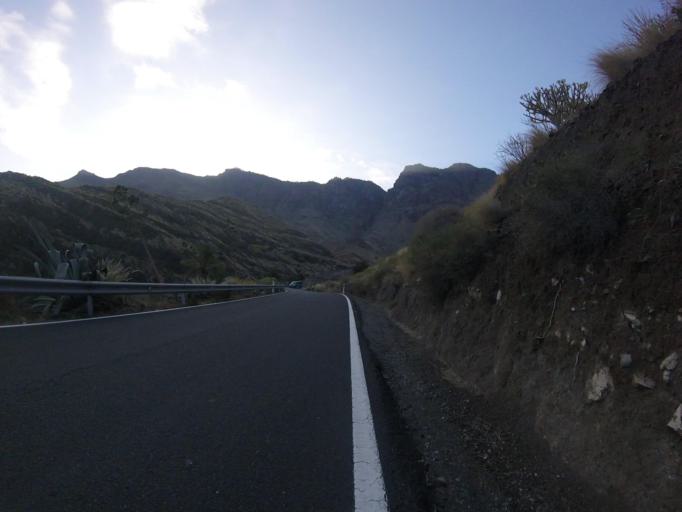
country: ES
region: Canary Islands
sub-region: Provincia de Las Palmas
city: Agaete
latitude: 28.0773
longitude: -15.7050
